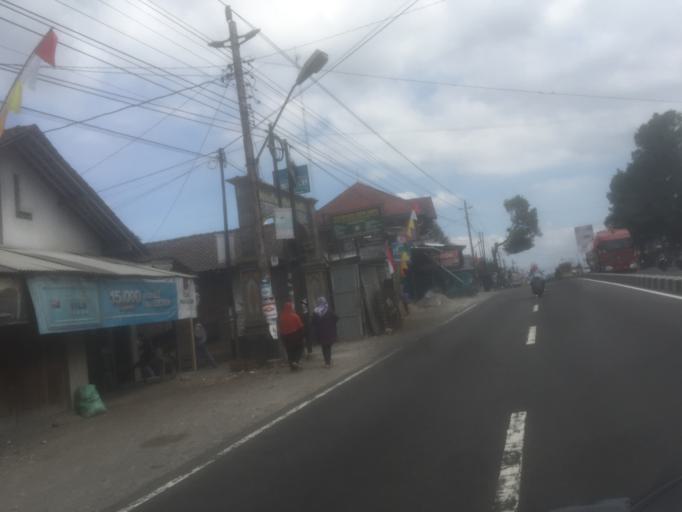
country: ID
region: Central Java
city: Muntilan
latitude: -7.6111
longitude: 110.3049
